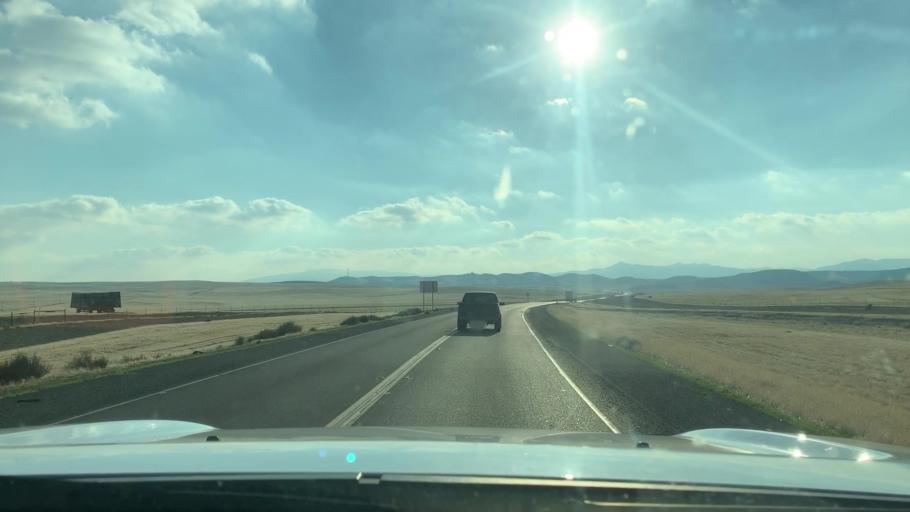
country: US
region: California
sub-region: Kings County
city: Avenal
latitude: 35.8828
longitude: -120.0506
